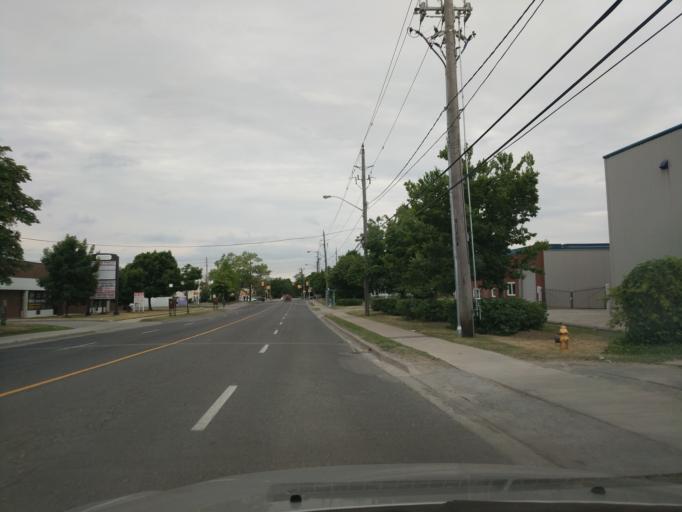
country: CA
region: Ontario
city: Markham
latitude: 43.8190
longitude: -79.3026
